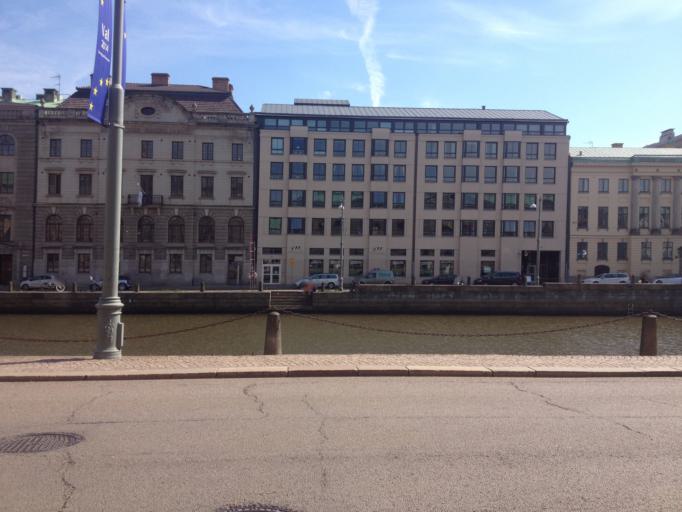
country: SE
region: Vaestra Goetaland
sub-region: Goteborg
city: Goeteborg
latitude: 57.7062
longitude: 11.9642
